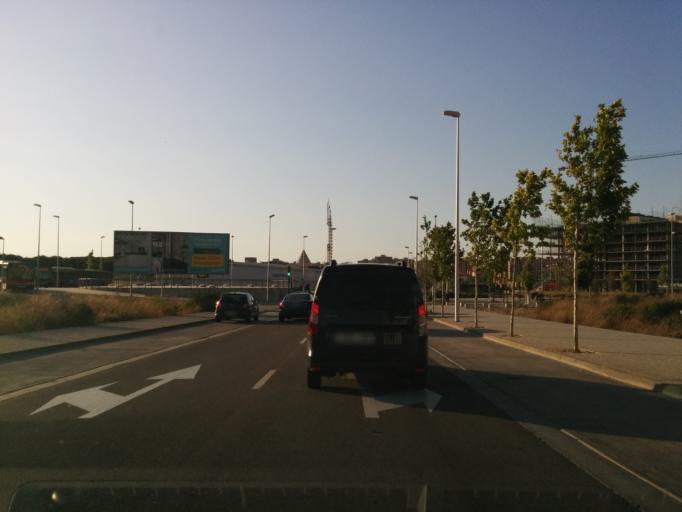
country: ES
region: Aragon
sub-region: Provincia de Zaragoza
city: Zaragoza
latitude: 41.6171
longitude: -0.8758
